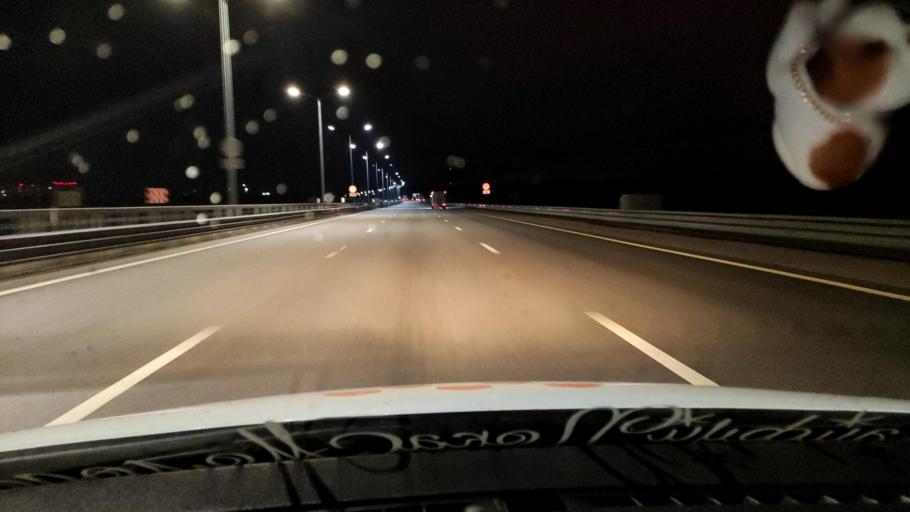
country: RU
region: Voronezj
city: Somovo
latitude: 51.7544
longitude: 39.3063
